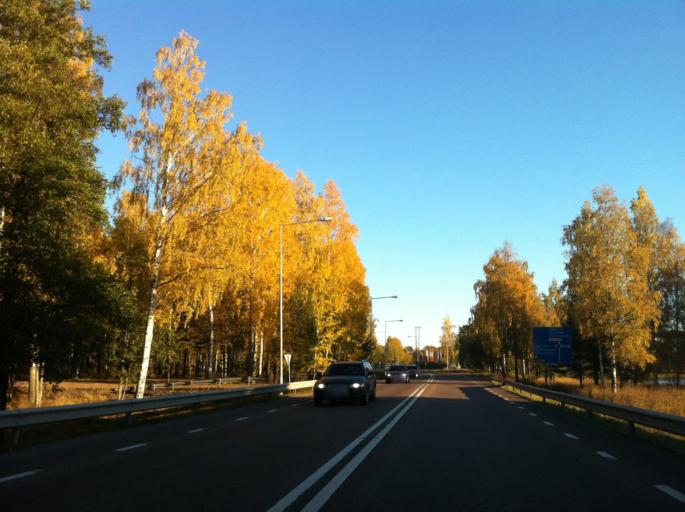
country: SE
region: Dalarna
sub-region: Faluns Kommun
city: Falun
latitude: 60.6276
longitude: 15.6056
